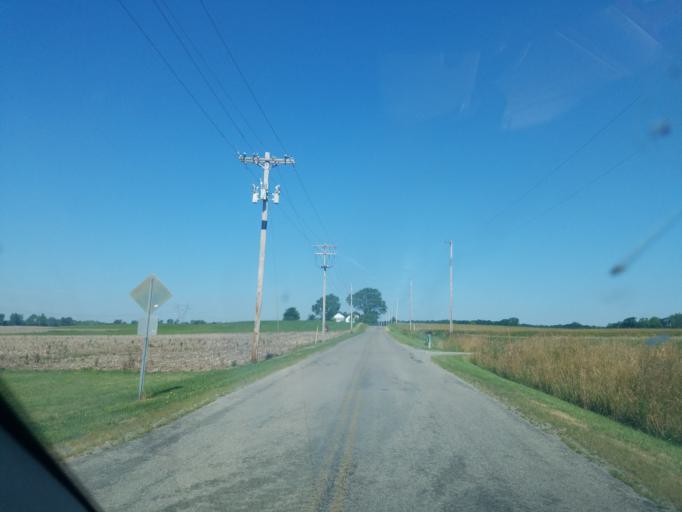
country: US
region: Ohio
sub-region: Logan County
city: Northwood
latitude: 40.4409
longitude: -83.6799
